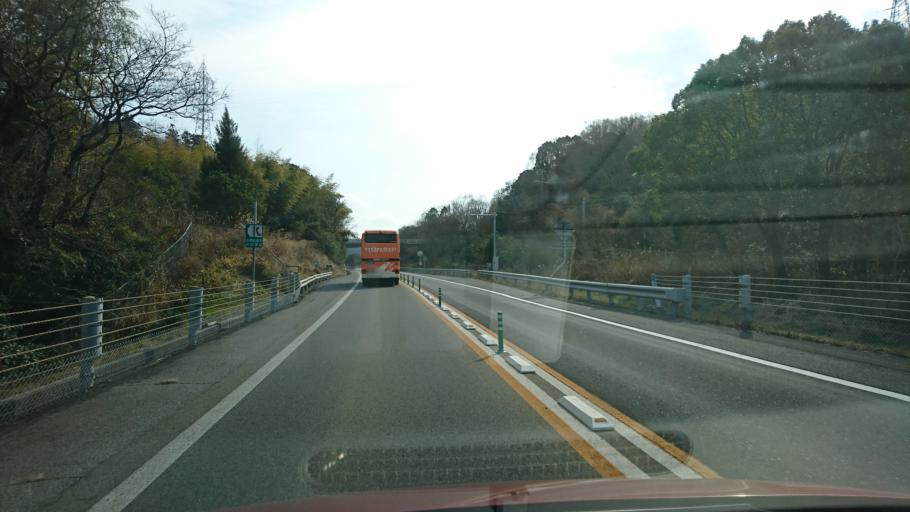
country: JP
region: Hiroshima
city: Innoshima
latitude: 34.2205
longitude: 133.0497
